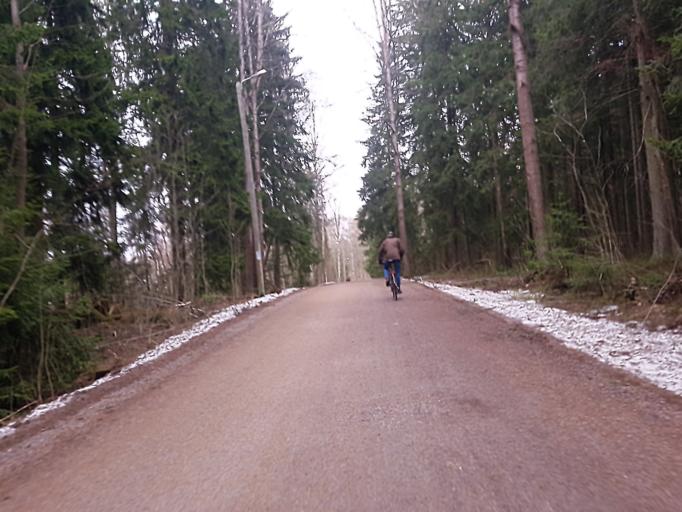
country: FI
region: Uusimaa
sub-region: Helsinki
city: Helsinki
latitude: 60.2262
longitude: 24.9182
